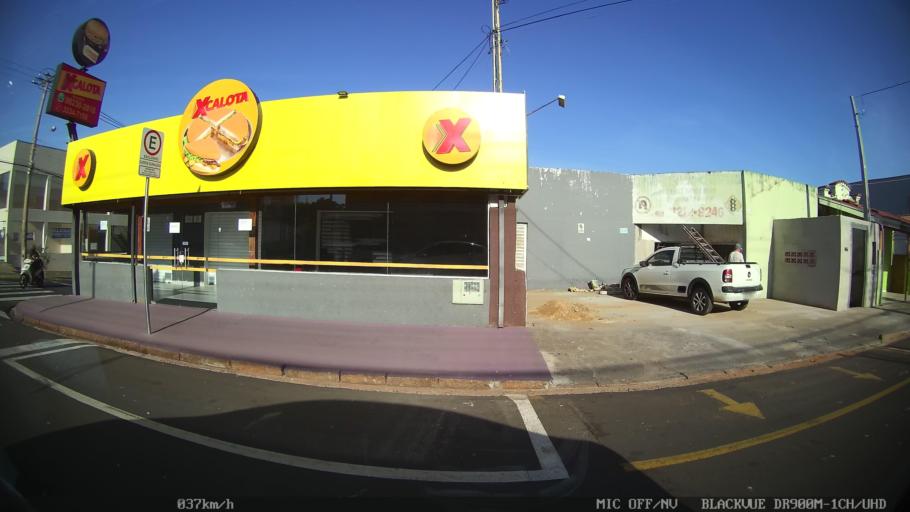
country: BR
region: Sao Paulo
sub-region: Sao Jose Do Rio Preto
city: Sao Jose do Rio Preto
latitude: -20.8086
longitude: -49.3885
